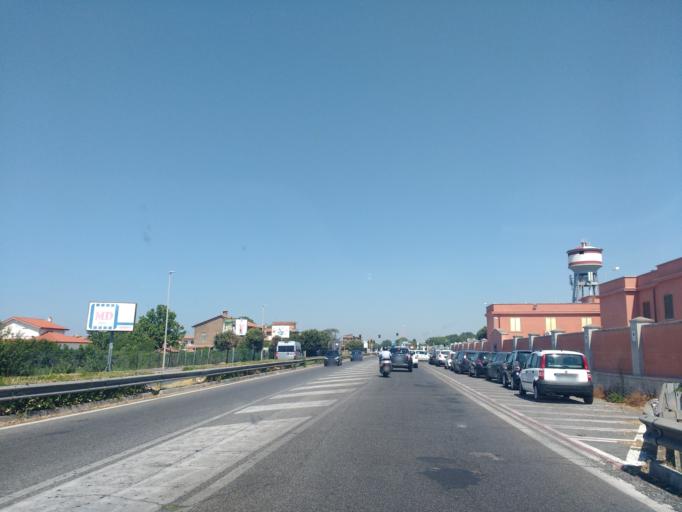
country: IT
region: Latium
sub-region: Citta metropolitana di Roma Capitale
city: Lido di Ostia
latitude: 41.7646
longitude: 12.2648
